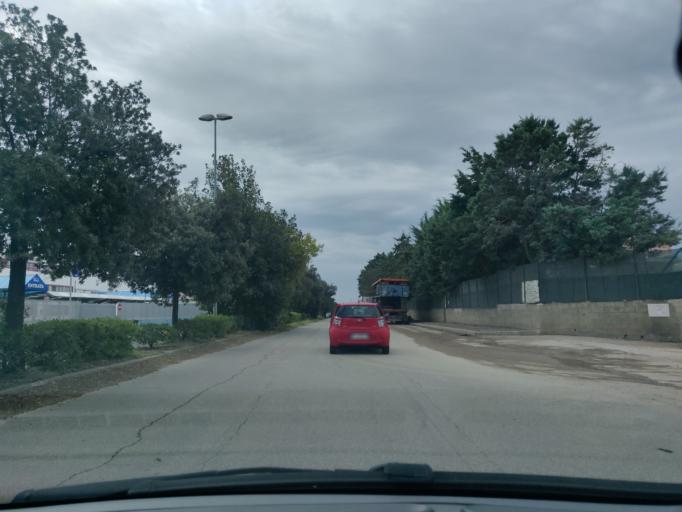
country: IT
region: Latium
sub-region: Citta metropolitana di Roma Capitale
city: Aurelia
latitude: 42.1191
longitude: 11.7785
